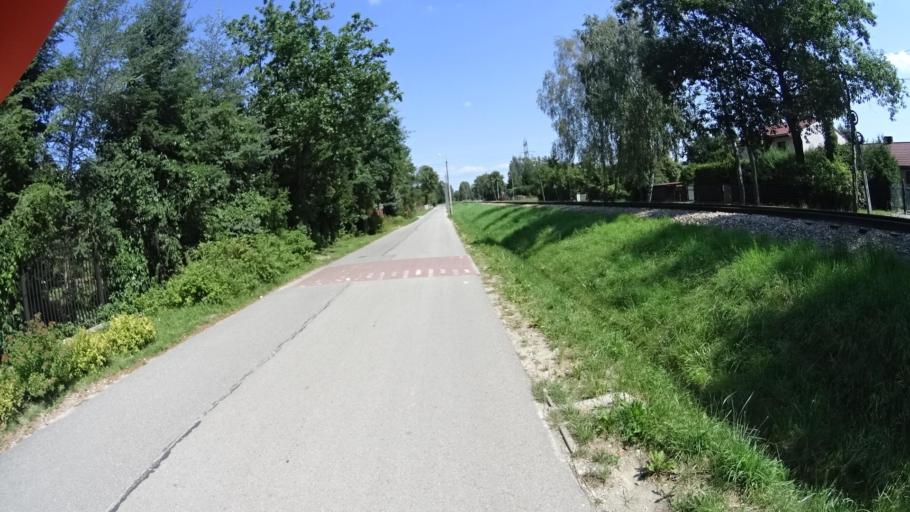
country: PL
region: Masovian Voivodeship
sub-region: Powiat piaseczynski
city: Tarczyn
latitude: 52.0017
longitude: 20.9064
